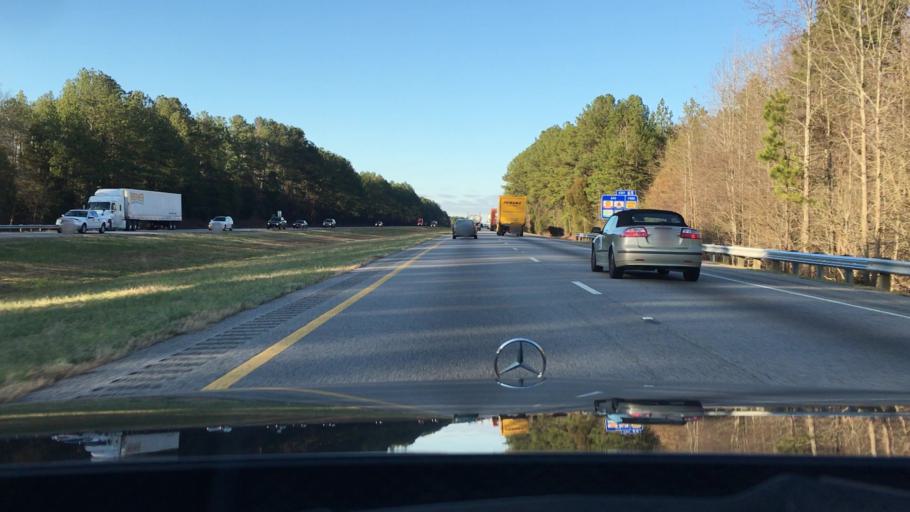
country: US
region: South Carolina
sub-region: Chester County
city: Eureka Mill
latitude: 34.7341
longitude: -81.0342
